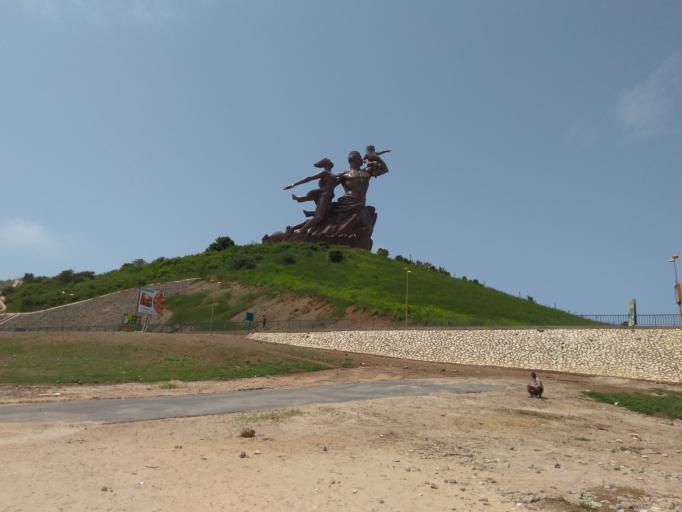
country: SN
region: Dakar
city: Mermoz Boabab
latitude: 14.7235
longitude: -17.4939
